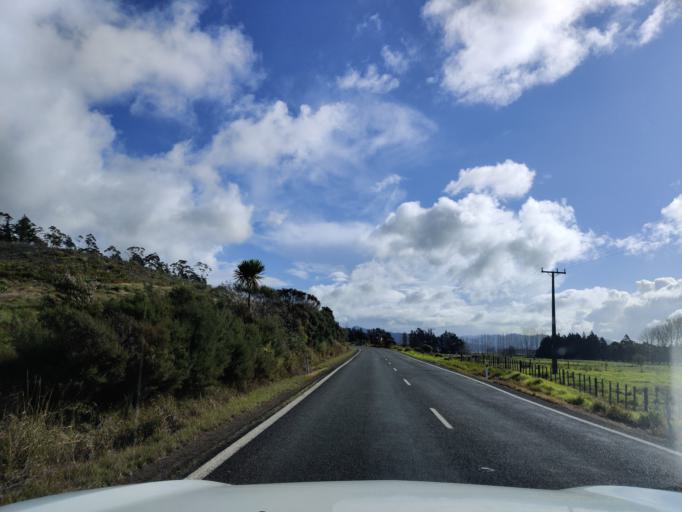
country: NZ
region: Waikato
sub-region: Thames-Coromandel District
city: Whitianga
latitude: -36.7486
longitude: 175.6767
